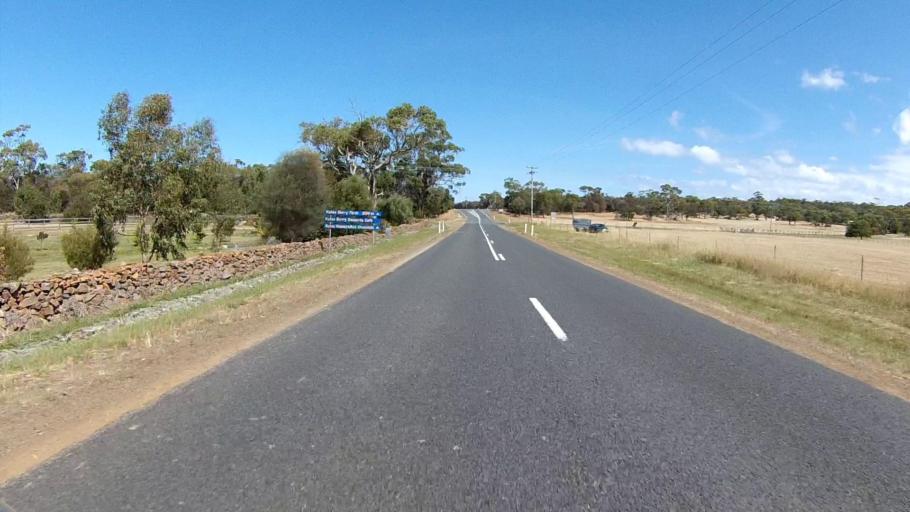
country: AU
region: Tasmania
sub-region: Sorell
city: Sorell
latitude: -42.1408
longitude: 148.0699
